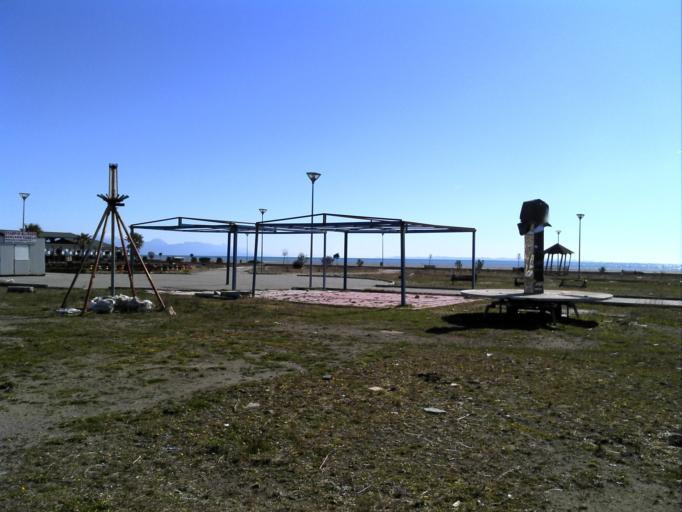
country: AL
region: Shkoder
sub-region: Rrethi i Shkodres
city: Velipoje
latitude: 41.8631
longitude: 19.4242
